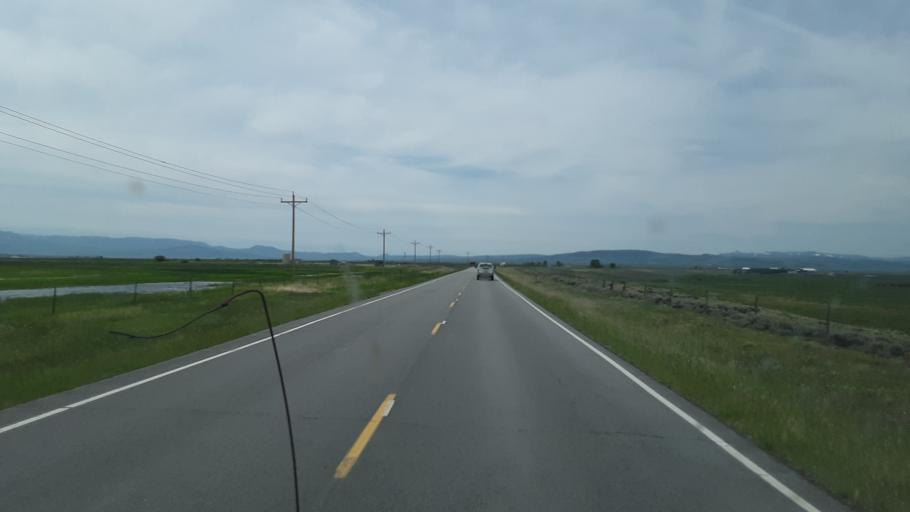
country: US
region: Colorado
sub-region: Jackson County
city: Walden
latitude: 40.6220
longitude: -106.3999
